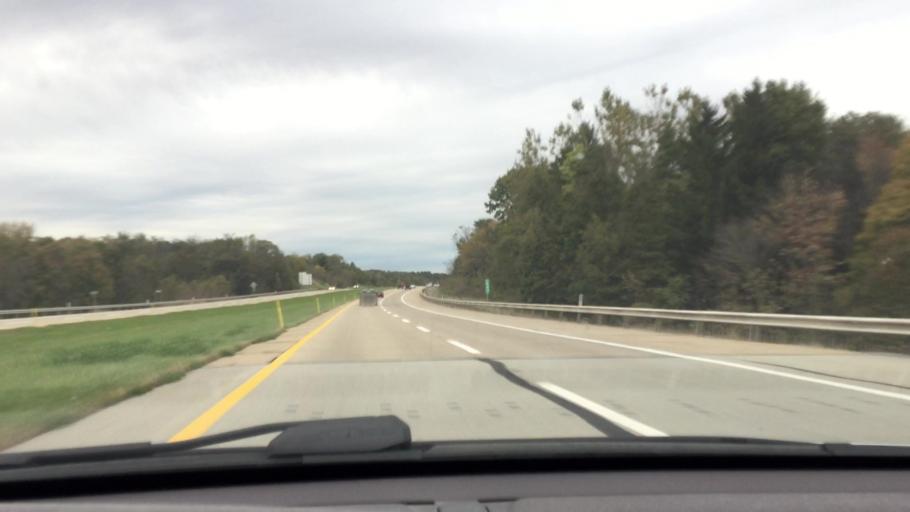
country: US
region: Pennsylvania
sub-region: Lawrence County
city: New Beaver
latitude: 40.8519
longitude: -80.3685
